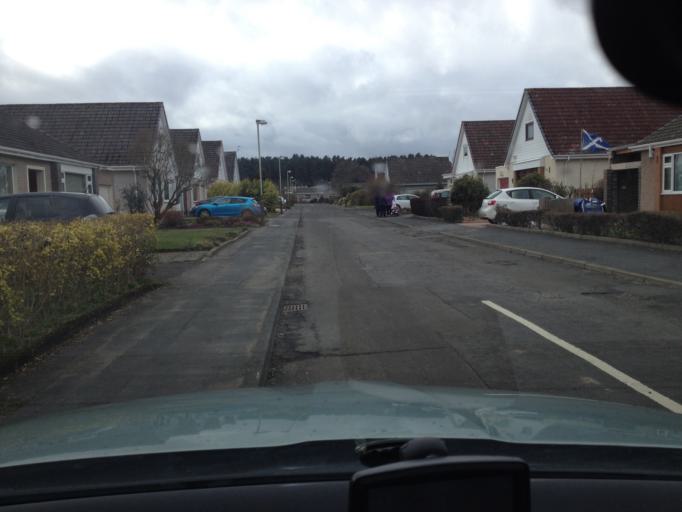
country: GB
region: Scotland
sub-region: Perth and Kinross
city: Scone
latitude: 56.4242
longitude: -3.4077
